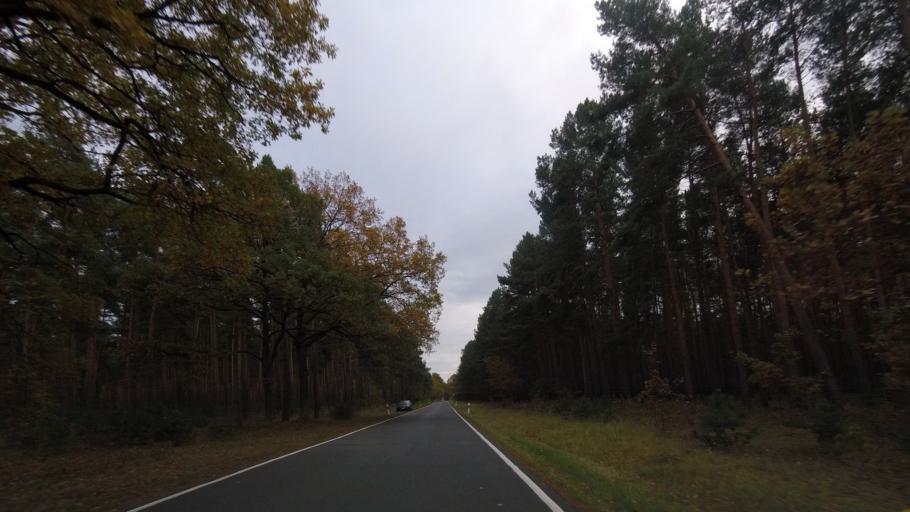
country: DE
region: Brandenburg
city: Treuenbrietzen
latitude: 52.1139
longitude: 12.8776
